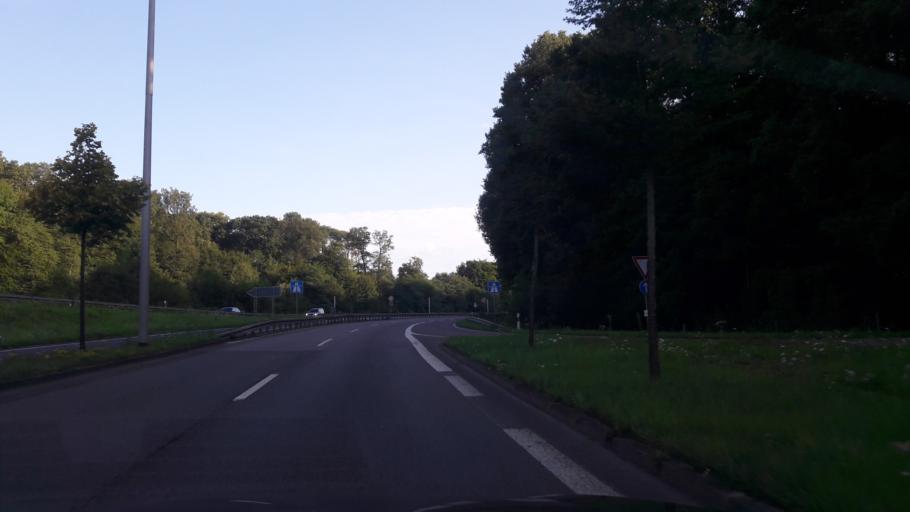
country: DE
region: Saarland
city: Saarbrucken
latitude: 49.2596
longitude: 6.9579
